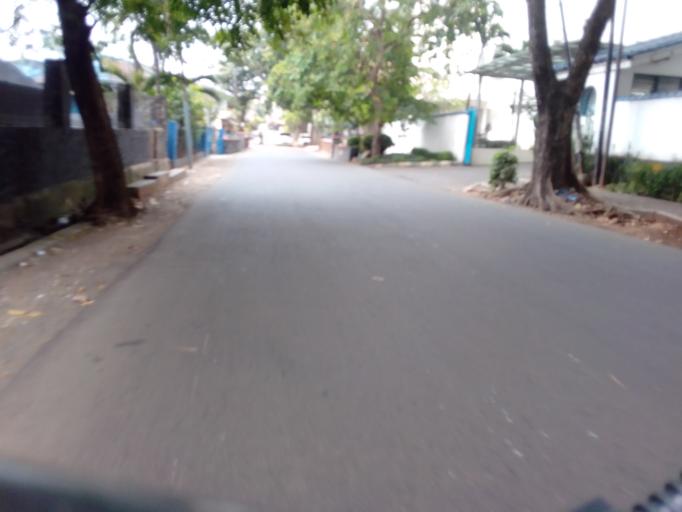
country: ID
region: Jakarta Raya
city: Jakarta
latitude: -6.2126
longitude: 106.8090
